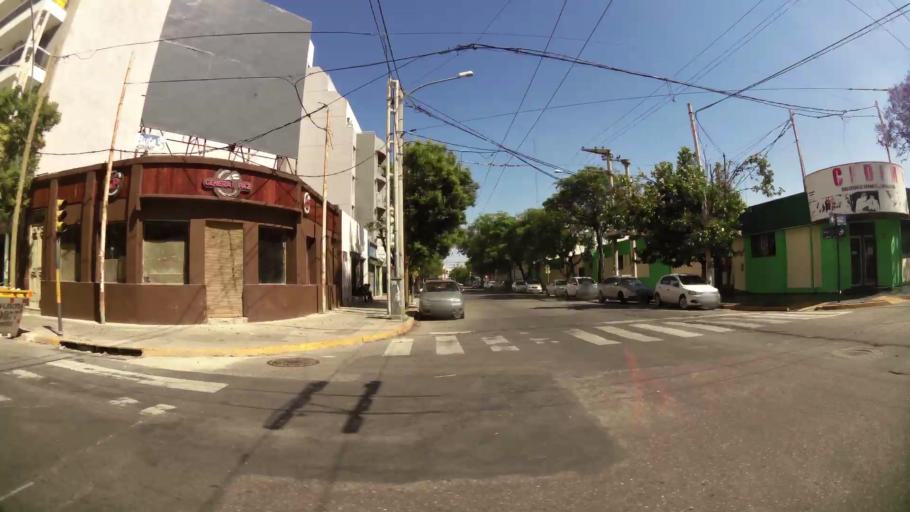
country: AR
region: Cordoba
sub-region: Departamento de Capital
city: Cordoba
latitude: -31.4131
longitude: -64.1634
